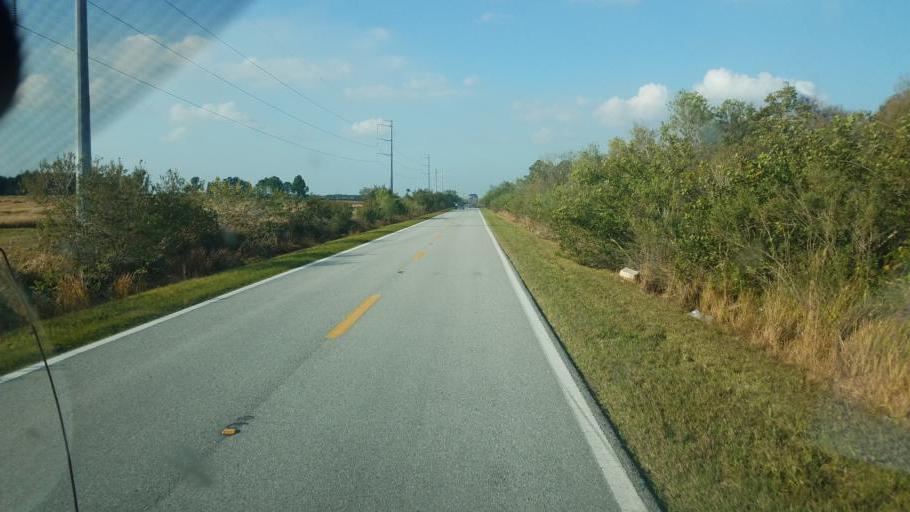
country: US
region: Florida
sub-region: Hardee County
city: Bowling Green
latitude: 27.6568
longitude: -81.9508
